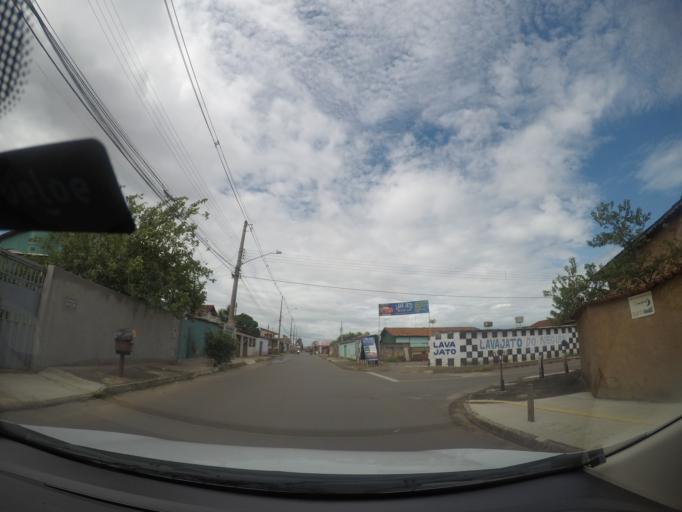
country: BR
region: Goias
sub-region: Aparecida De Goiania
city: Aparecida de Goiania
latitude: -16.7584
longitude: -49.3498
